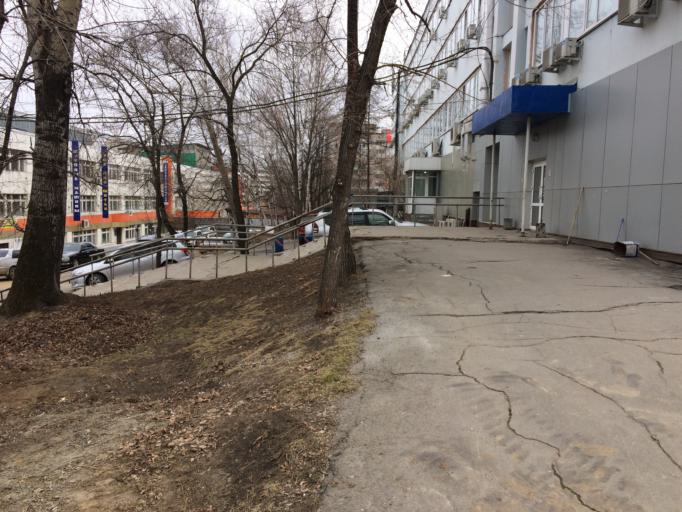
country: RU
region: Khabarovsk Krai
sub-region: Khabarovskiy Rayon
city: Khabarovsk
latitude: 48.4840
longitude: 135.0937
